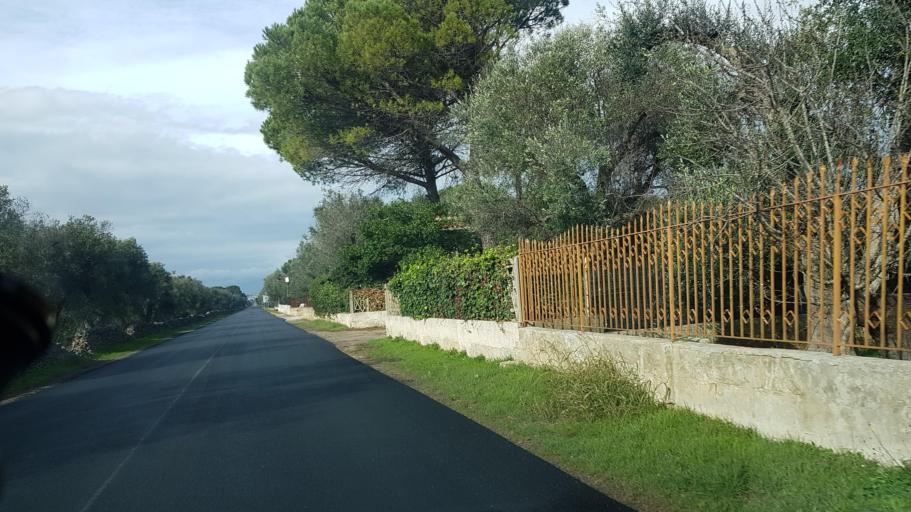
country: IT
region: Apulia
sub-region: Provincia di Brindisi
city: Oria
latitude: 40.4820
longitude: 17.6845
